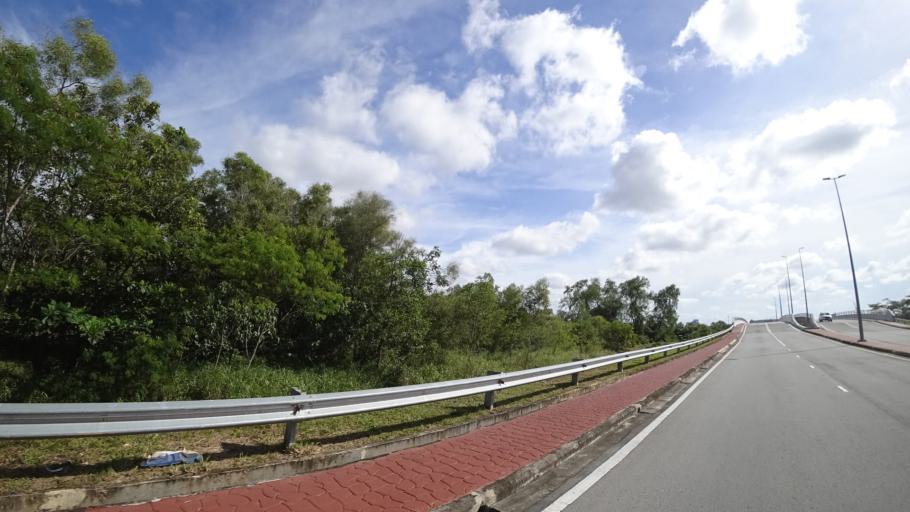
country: BN
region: Brunei and Muara
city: Bandar Seri Begawan
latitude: 4.9174
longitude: 114.9264
